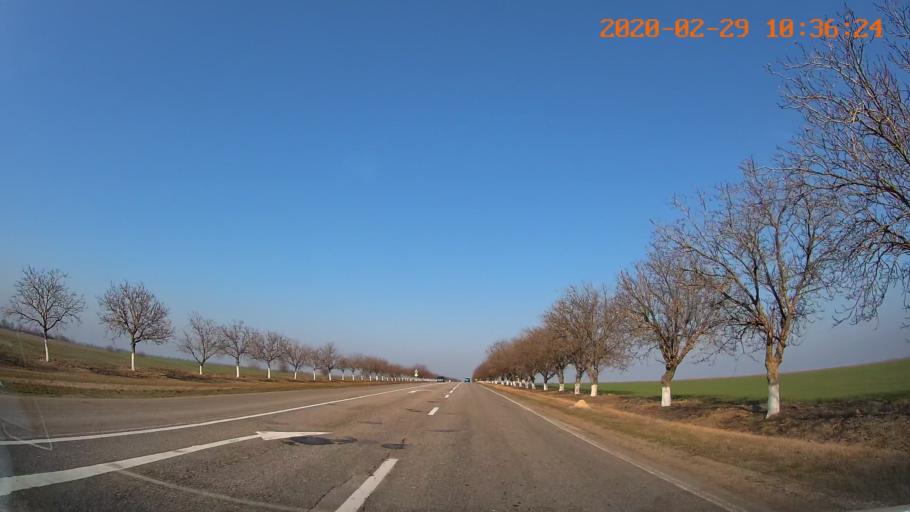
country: MD
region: Anenii Noi
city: Varnita
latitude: 46.9953
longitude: 29.5058
